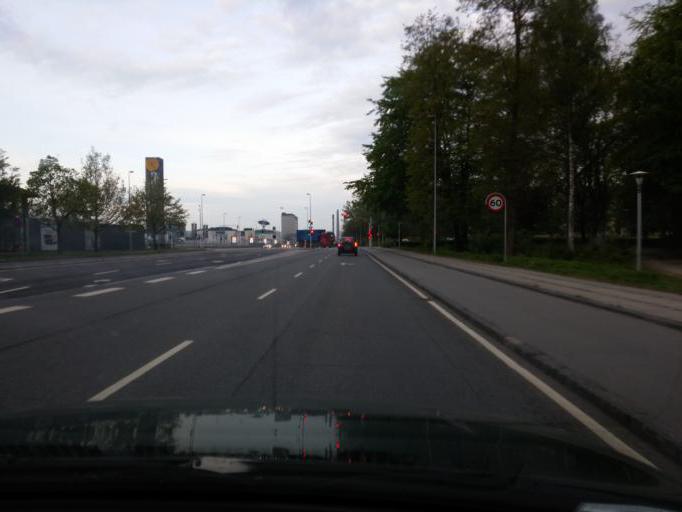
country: DK
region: South Denmark
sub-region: Odense Kommune
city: Neder Holluf
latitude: 55.3878
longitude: 10.4285
